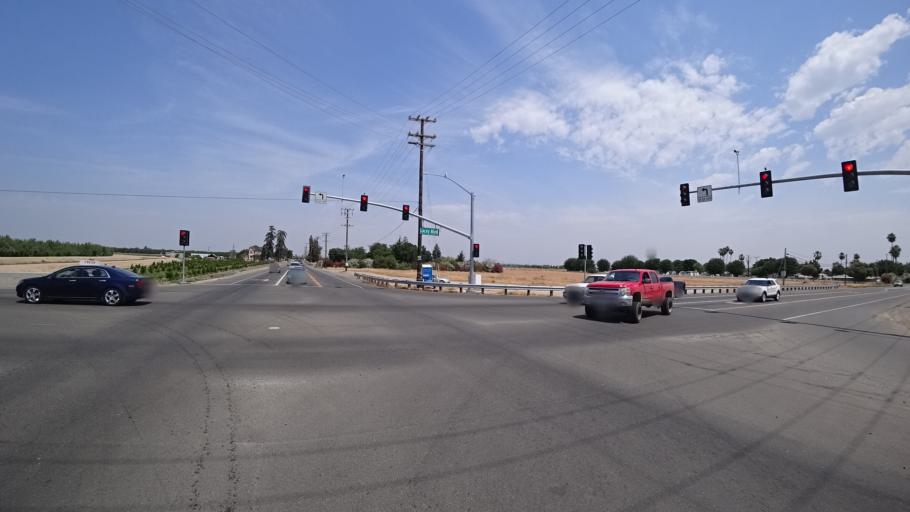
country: US
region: California
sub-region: Kings County
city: Armona
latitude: 36.3280
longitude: -119.6910
